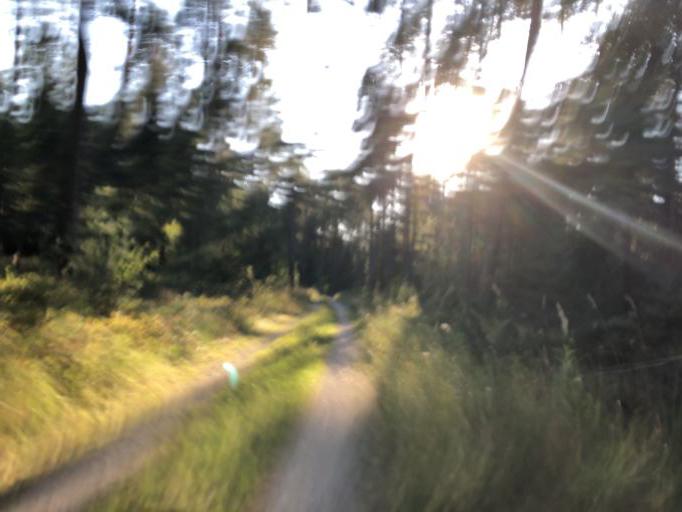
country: DE
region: Bavaria
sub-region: Regierungsbezirk Mittelfranken
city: Uttenreuth
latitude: 49.5666
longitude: 11.0804
